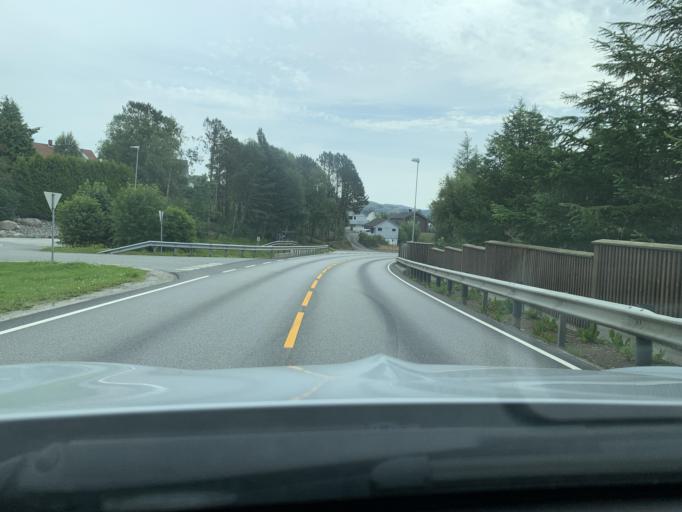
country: NO
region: Rogaland
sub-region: Sandnes
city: Sandnes
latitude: 58.7841
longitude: 5.7108
